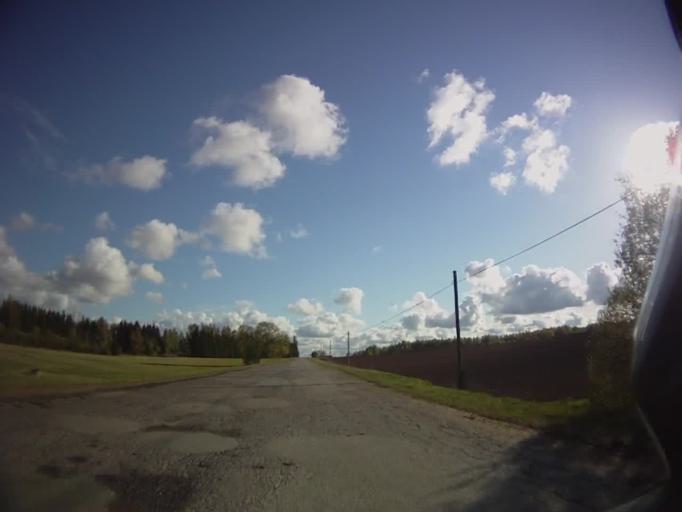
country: LV
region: Sigulda
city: Sigulda
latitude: 57.1649
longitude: 24.9071
